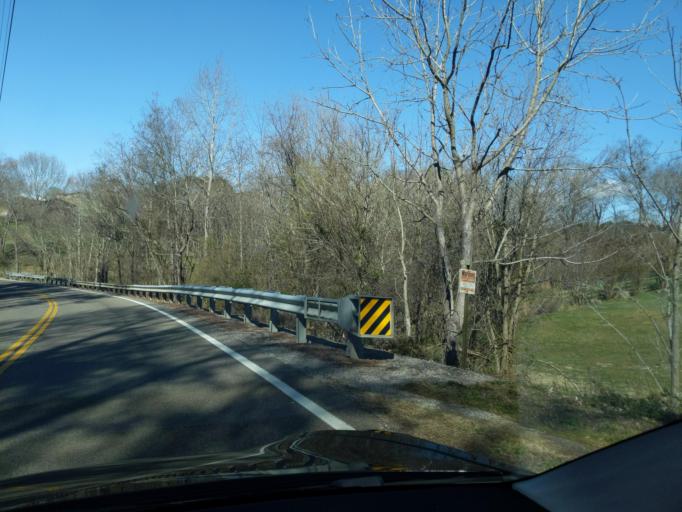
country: US
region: Tennessee
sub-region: Jefferson County
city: Dandridge
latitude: 35.9840
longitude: -83.4683
